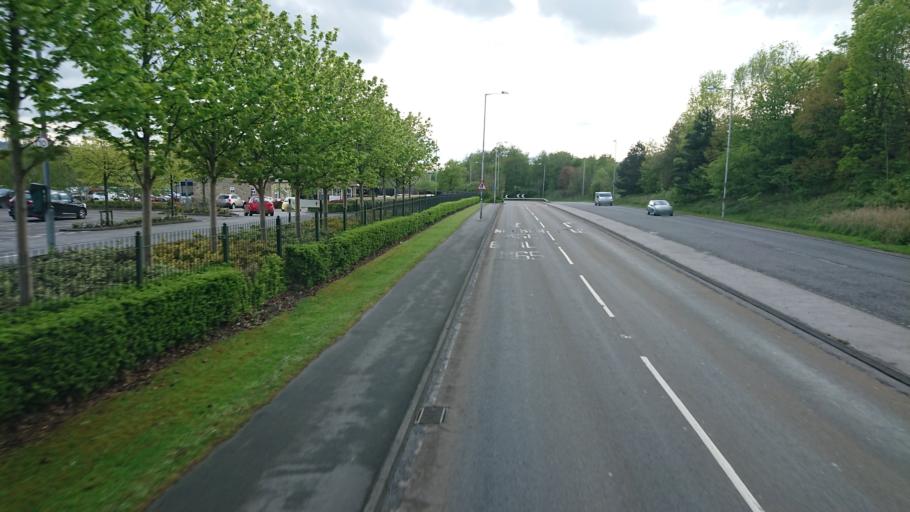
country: GB
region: England
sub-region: Lancashire
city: Colne
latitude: 53.8553
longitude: -2.1888
